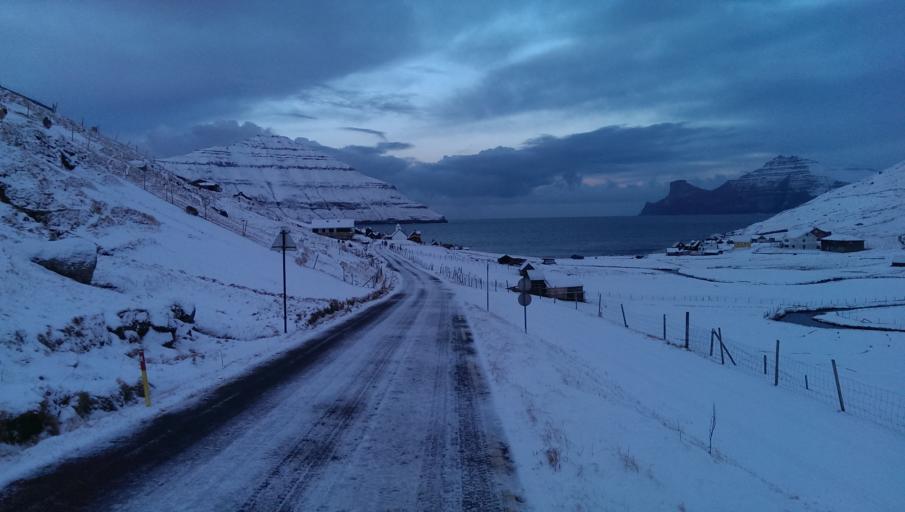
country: FO
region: Eysturoy
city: Fuglafjordur
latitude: 62.2795
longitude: -6.9139
